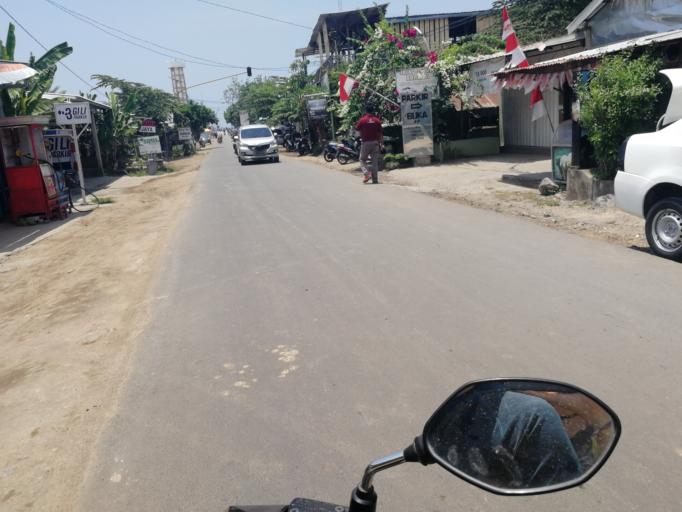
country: ID
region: West Nusa Tenggara
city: Pemenang
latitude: -8.3953
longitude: 116.0999
